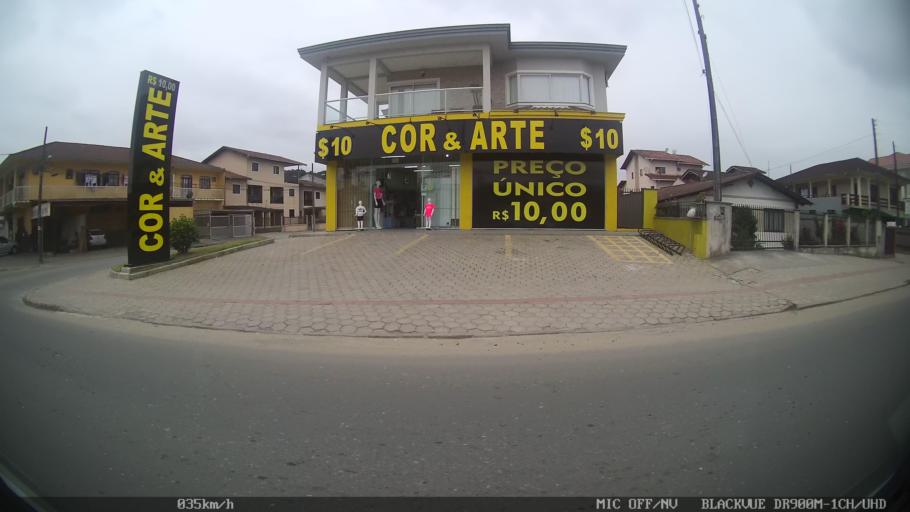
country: BR
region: Santa Catarina
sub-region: Joinville
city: Joinville
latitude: -26.3625
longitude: -48.8296
